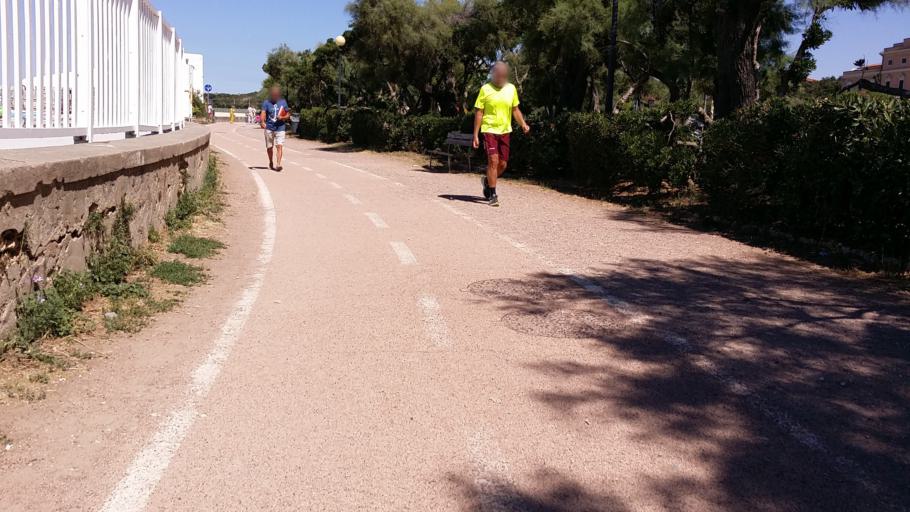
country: IT
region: Tuscany
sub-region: Provincia di Livorno
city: Livorno
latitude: 43.5152
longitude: 10.3168
